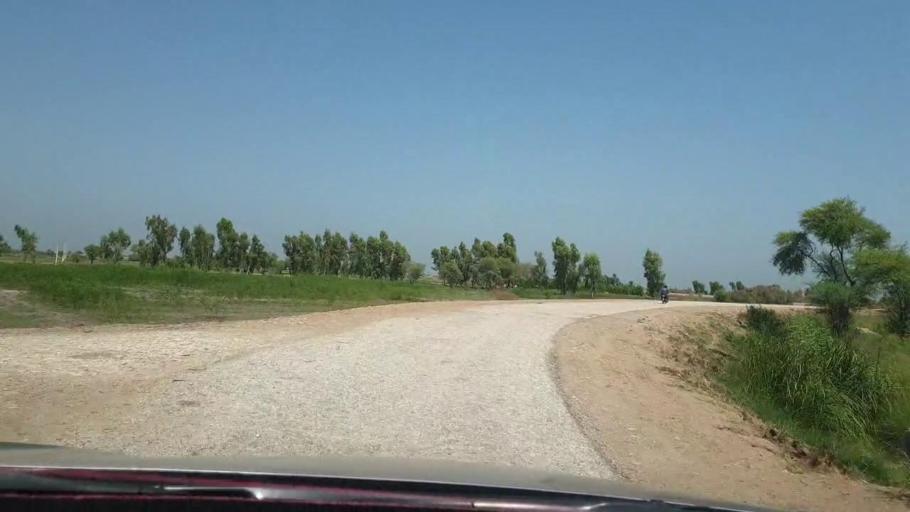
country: PK
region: Sindh
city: Warah
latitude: 27.5372
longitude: 67.7363
